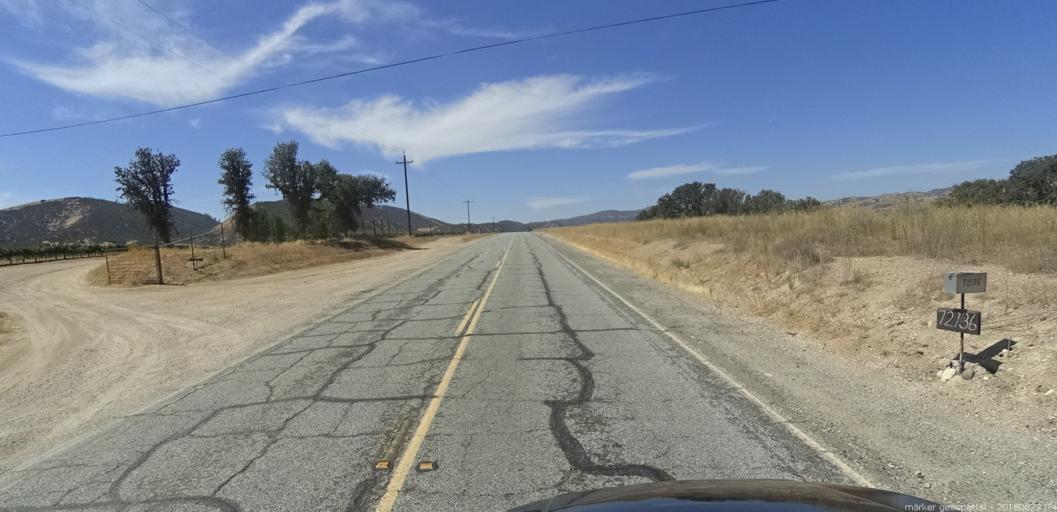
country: US
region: California
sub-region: San Luis Obispo County
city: Lake Nacimiento
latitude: 35.8791
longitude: -120.8973
